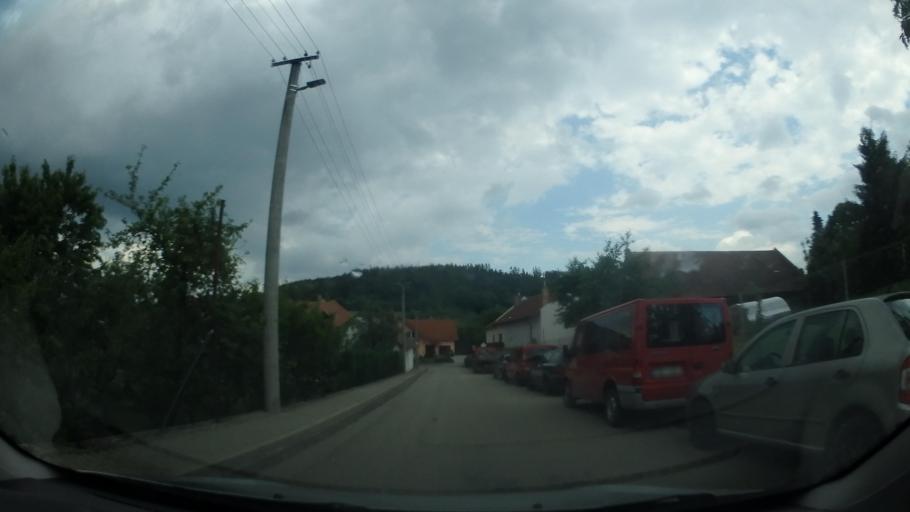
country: CZ
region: South Moravian
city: Svitavka
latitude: 49.4650
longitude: 16.6046
